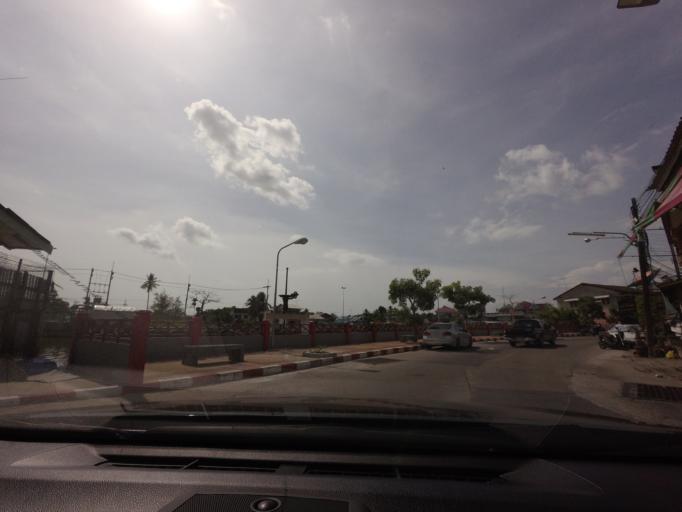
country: TH
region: Pattani
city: Pattani
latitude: 6.8635
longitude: 101.2517
